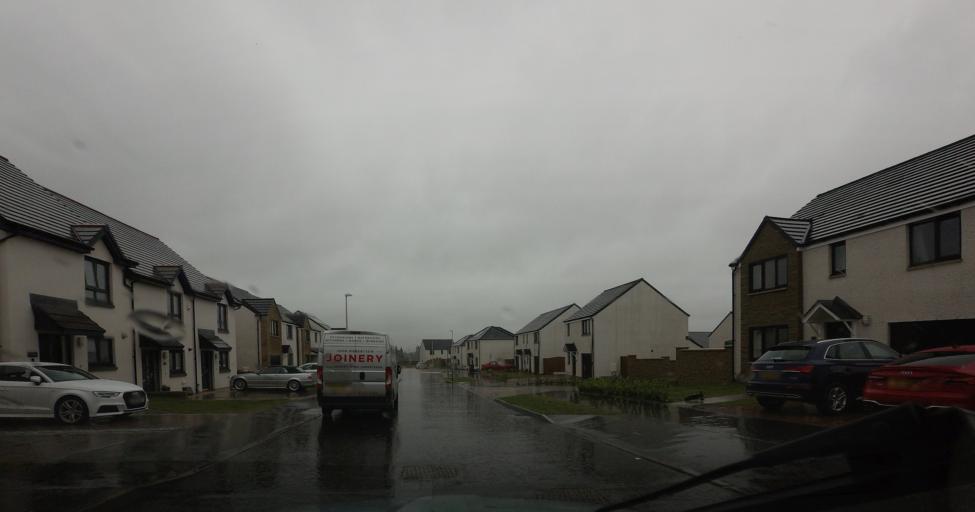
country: GB
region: Scotland
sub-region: Angus
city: Muirhead
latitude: 56.4738
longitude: -3.0684
